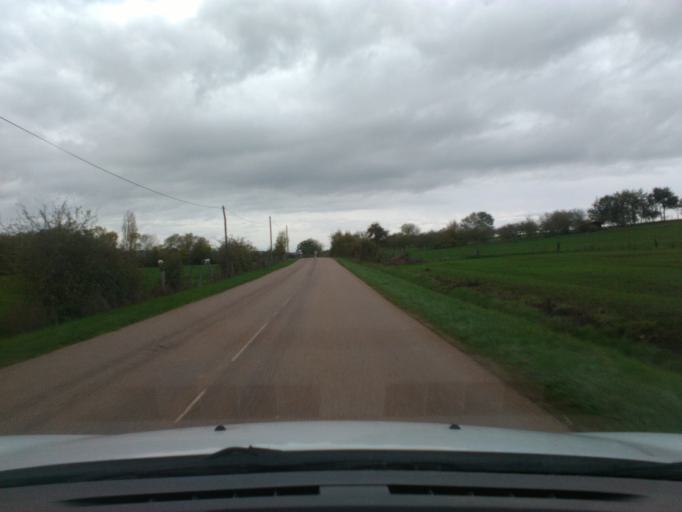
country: FR
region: Lorraine
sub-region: Departement des Vosges
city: Mirecourt
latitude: 48.3503
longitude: 6.0927
